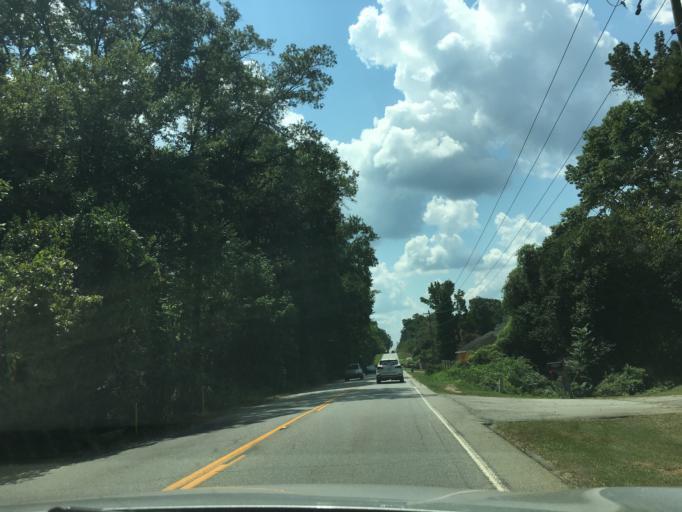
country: US
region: South Carolina
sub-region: Richland County
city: Lake Murray of Richland
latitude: 34.1196
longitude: -81.2290
